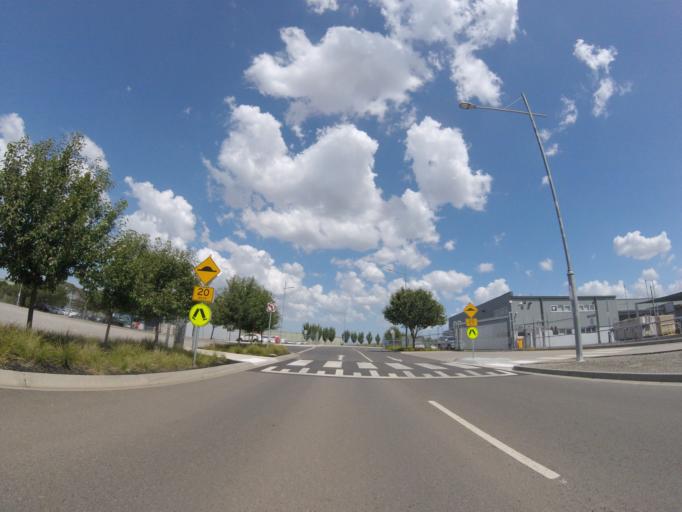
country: AU
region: Victoria
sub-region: Moreland
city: Oak Park
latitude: -37.7216
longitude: 144.9030
